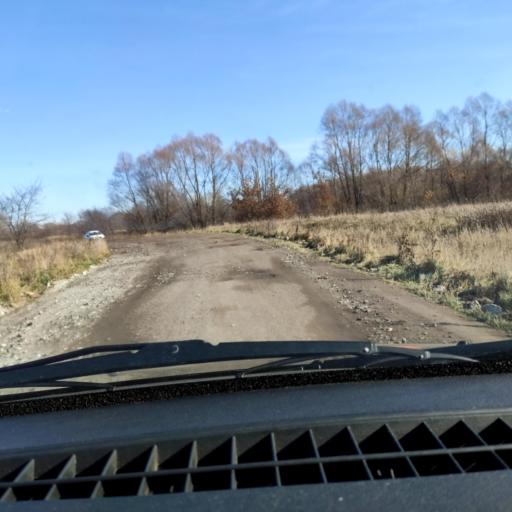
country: RU
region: Bashkortostan
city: Avdon
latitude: 54.4938
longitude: 55.8561
